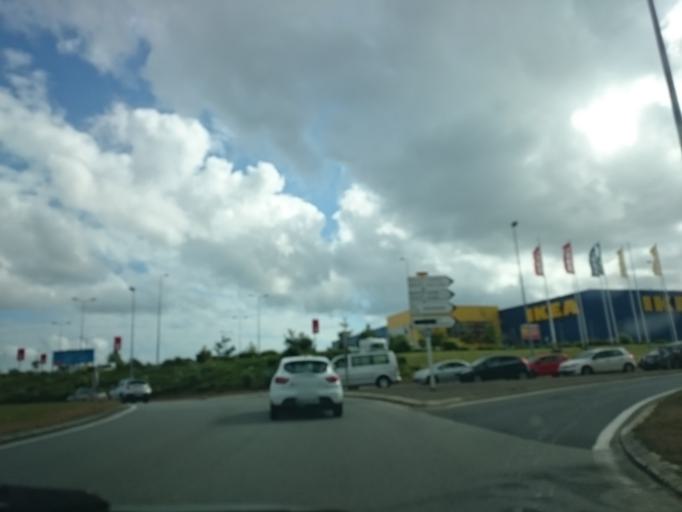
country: FR
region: Brittany
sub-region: Departement du Finistere
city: Gouesnou
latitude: 48.4190
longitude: -4.4398
